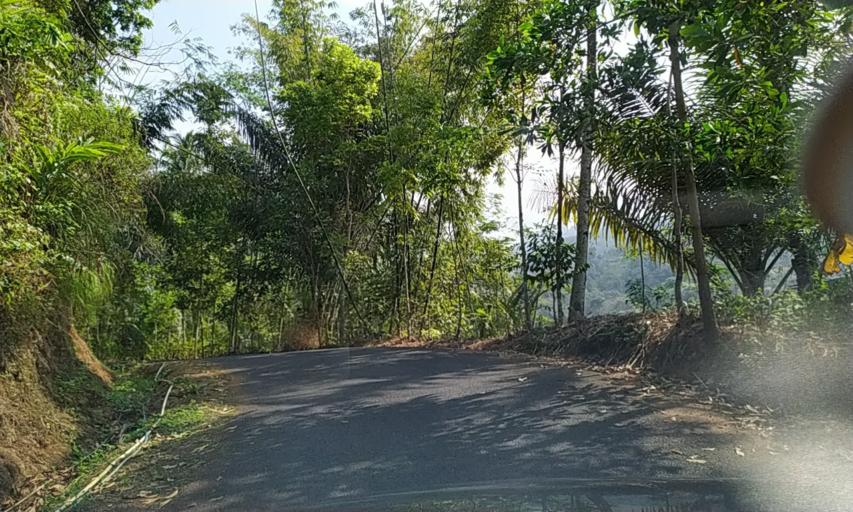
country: ID
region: Central Java
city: Kujang
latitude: -7.1964
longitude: 108.5935
